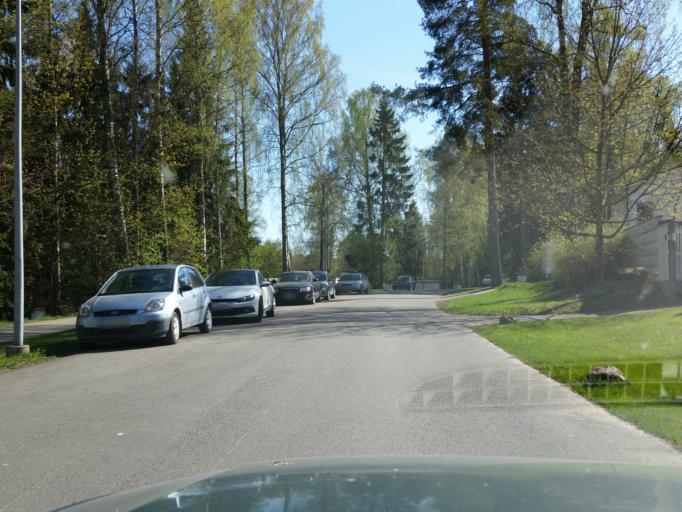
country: FI
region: Uusimaa
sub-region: Helsinki
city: Koukkuniemi
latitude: 60.1713
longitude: 24.7928
